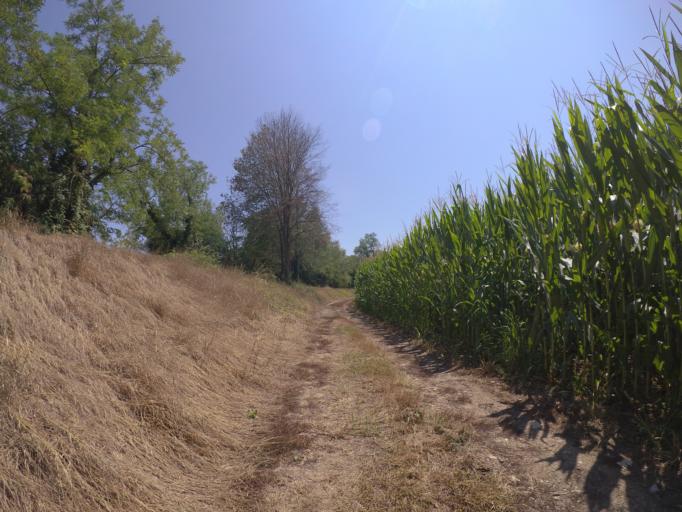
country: IT
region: Friuli Venezia Giulia
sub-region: Provincia di Udine
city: Varmo
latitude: 45.9252
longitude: 13.0129
